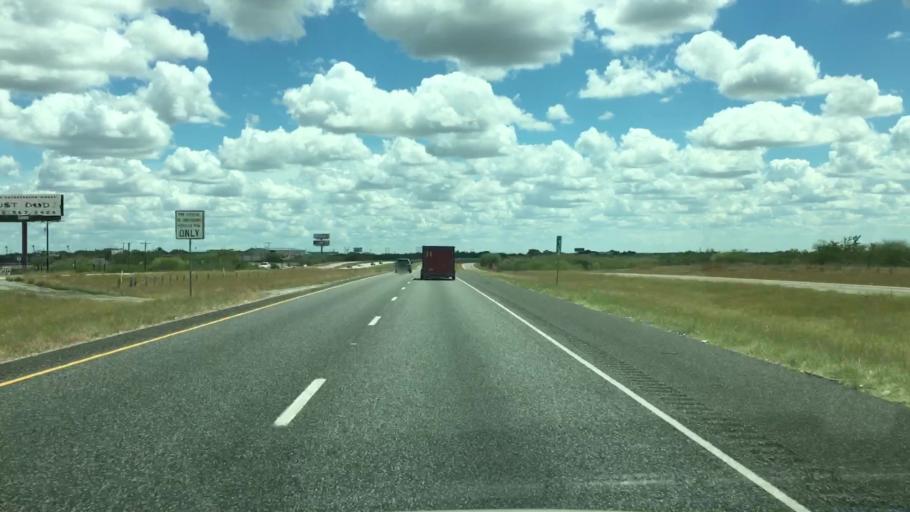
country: US
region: Texas
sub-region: Atascosa County
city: Pleasanton
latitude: 28.8907
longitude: -98.4098
